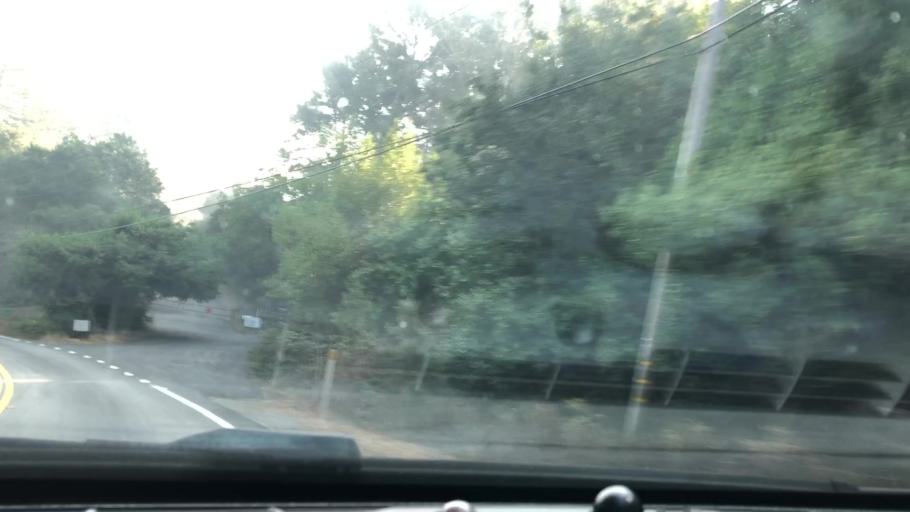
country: US
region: California
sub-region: Alameda County
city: Berkeley
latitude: 37.8872
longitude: -122.2468
